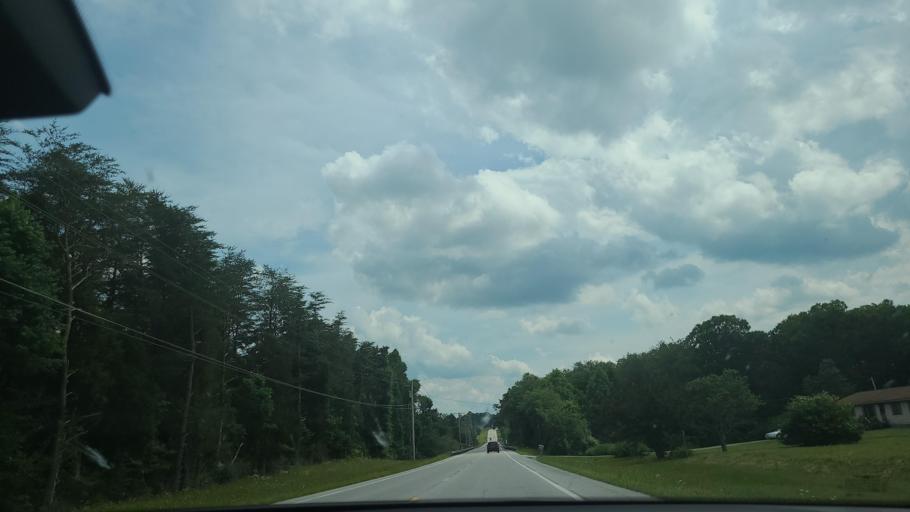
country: US
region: Tennessee
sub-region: Cumberland County
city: Lake Tansi
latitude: 35.8122
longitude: -85.0202
